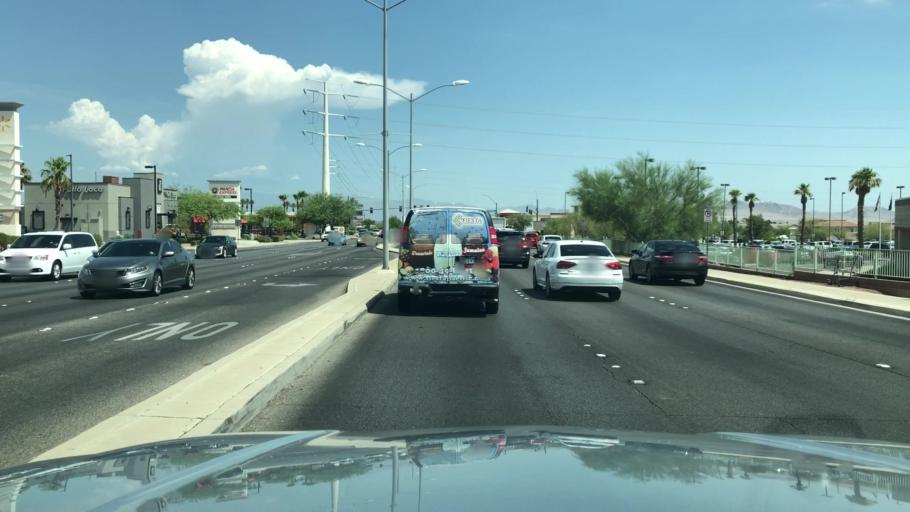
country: US
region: Nevada
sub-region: Clark County
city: Whitney
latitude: 36.0398
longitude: -115.0468
